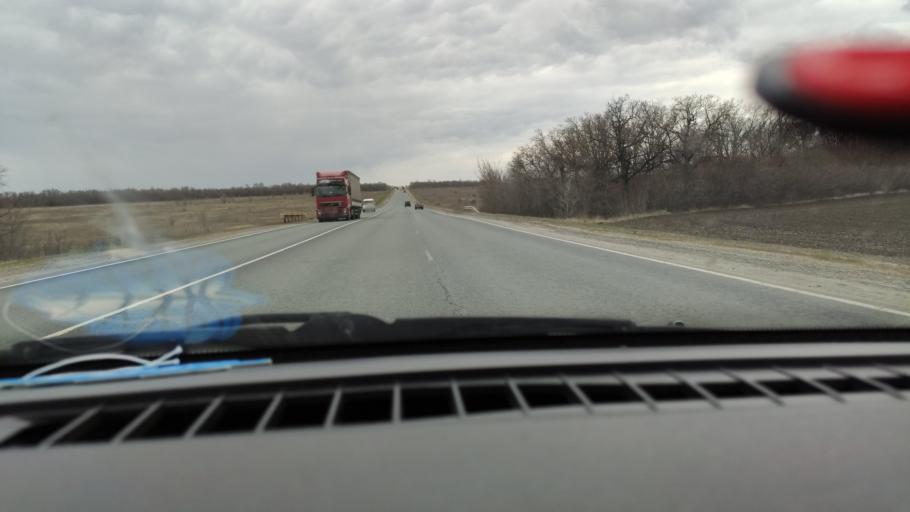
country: RU
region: Saratov
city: Sinodskoye
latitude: 51.9131
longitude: 46.5548
